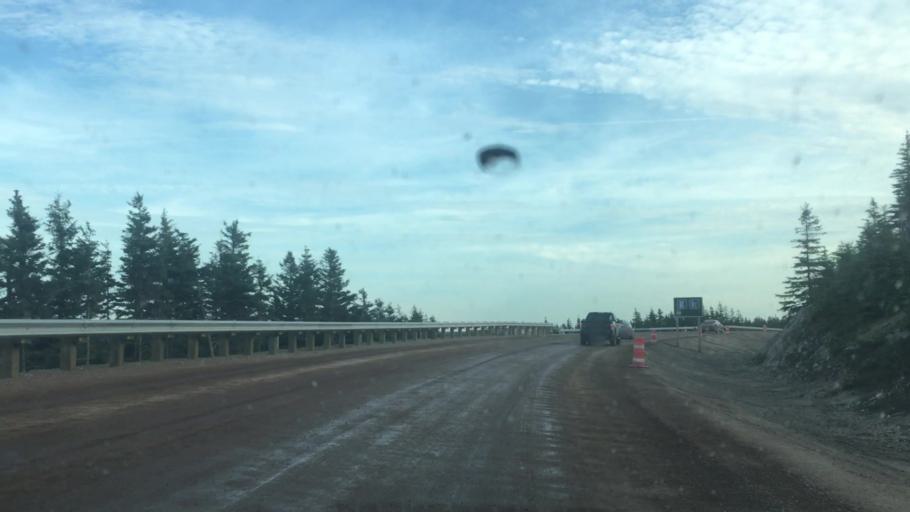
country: CA
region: Nova Scotia
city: Sydney Mines
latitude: 46.8044
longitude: -60.8437
